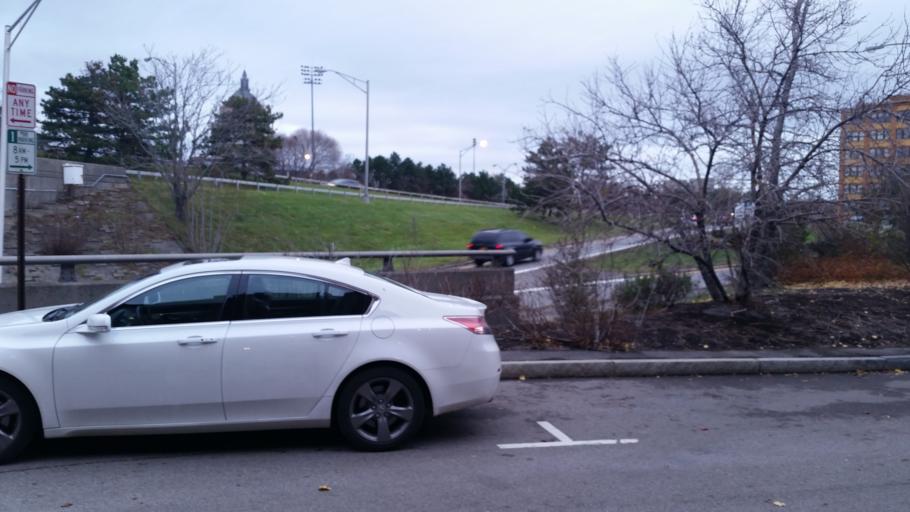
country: US
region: New York
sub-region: Monroe County
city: Rochester
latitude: 43.1559
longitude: -77.6196
